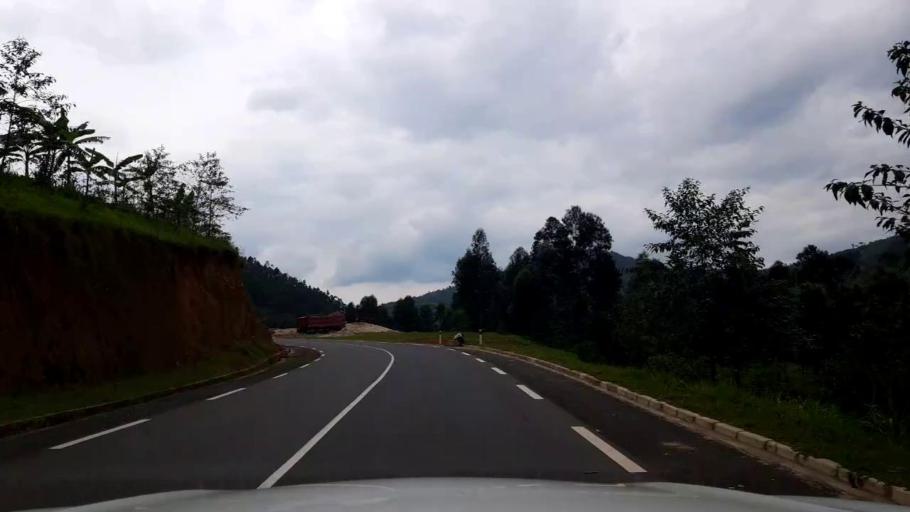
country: RW
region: Western Province
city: Kibuye
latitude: -1.9178
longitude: 29.3690
